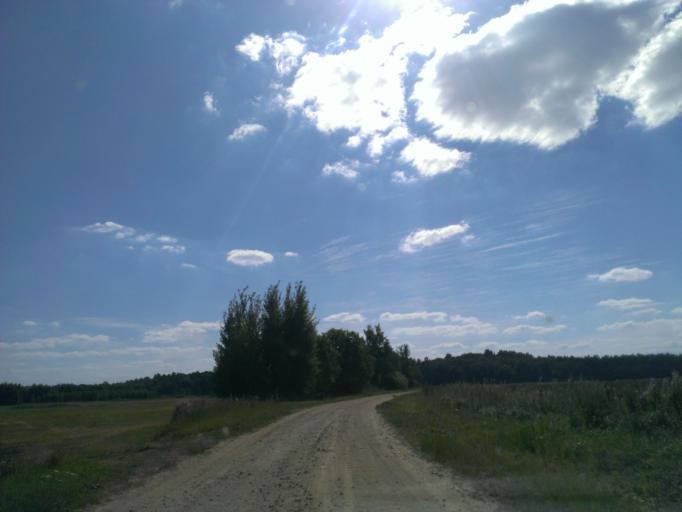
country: LV
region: Riga
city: Jaunciems
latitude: 57.0843
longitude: 24.2114
